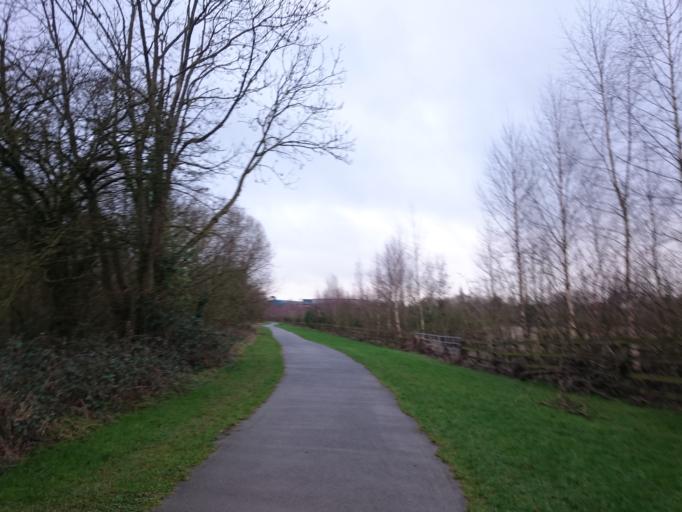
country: IE
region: Leinster
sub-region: Kilkenny
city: Kilkenny
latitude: 52.6735
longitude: -7.2607
